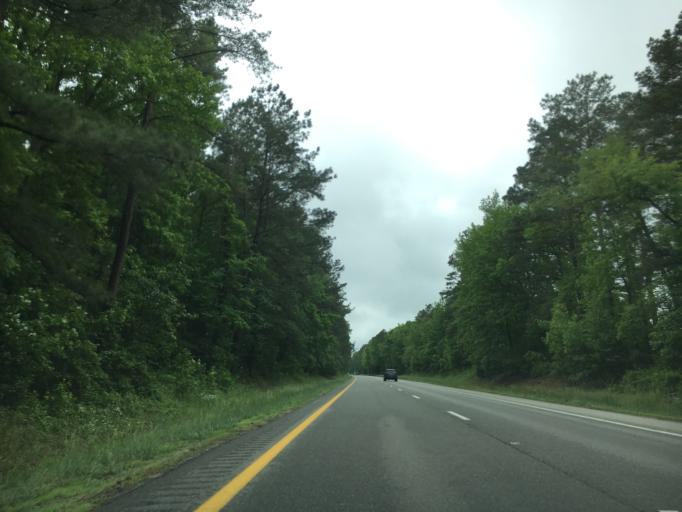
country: US
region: Virginia
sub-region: Brunswick County
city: Lawrenceville
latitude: 36.9033
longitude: -77.7915
